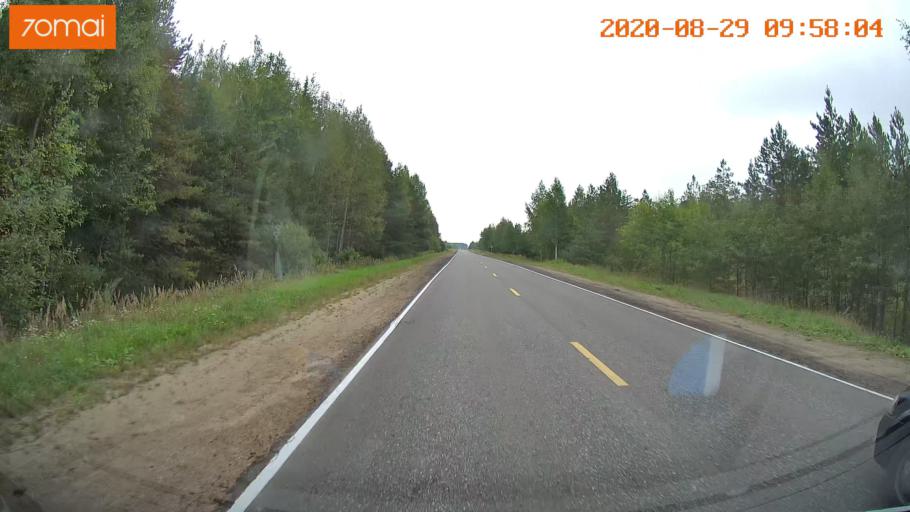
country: RU
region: Ivanovo
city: Zarechnyy
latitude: 57.4146
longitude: 42.3298
